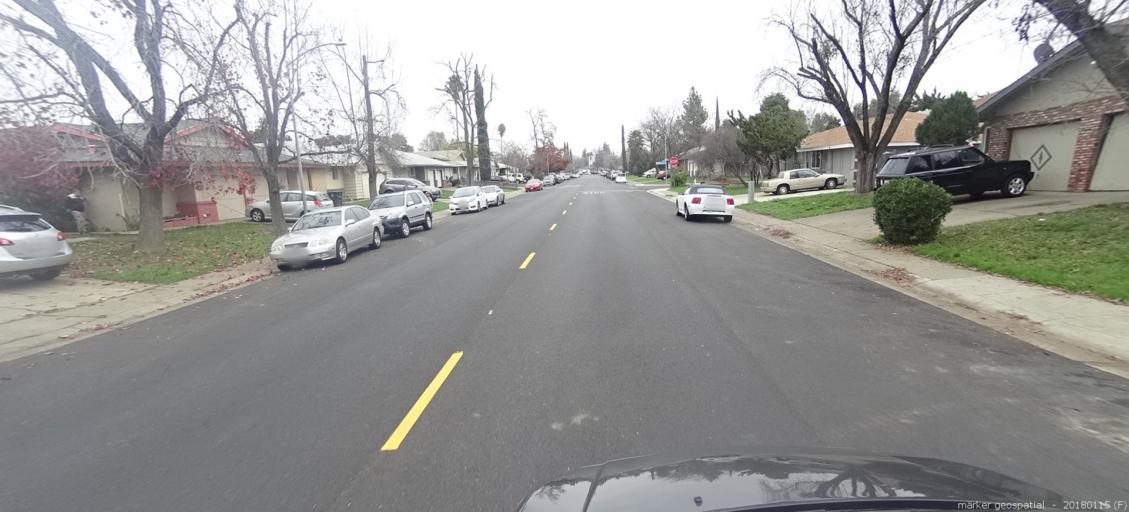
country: US
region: California
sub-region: Sacramento County
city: Rancho Cordova
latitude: 38.5878
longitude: -121.3037
